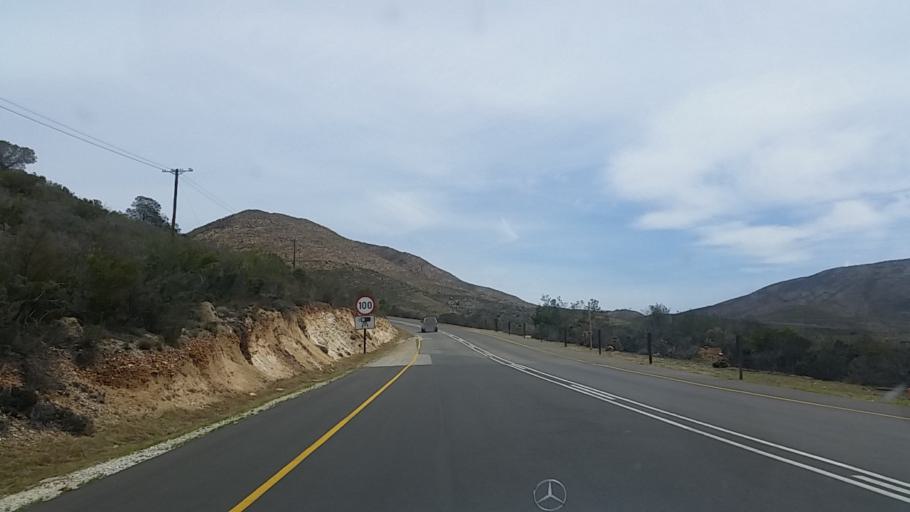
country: ZA
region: Western Cape
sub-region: Eden District Municipality
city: George
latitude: -33.8195
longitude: 22.3538
